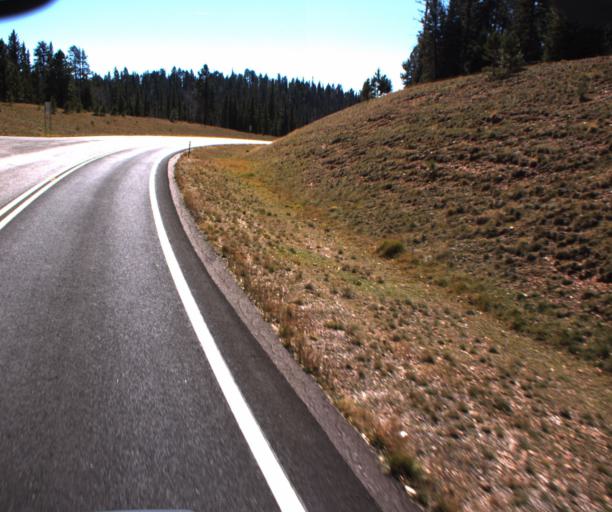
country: US
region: Arizona
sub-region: Coconino County
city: Grand Canyon
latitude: 36.4481
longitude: -112.1293
